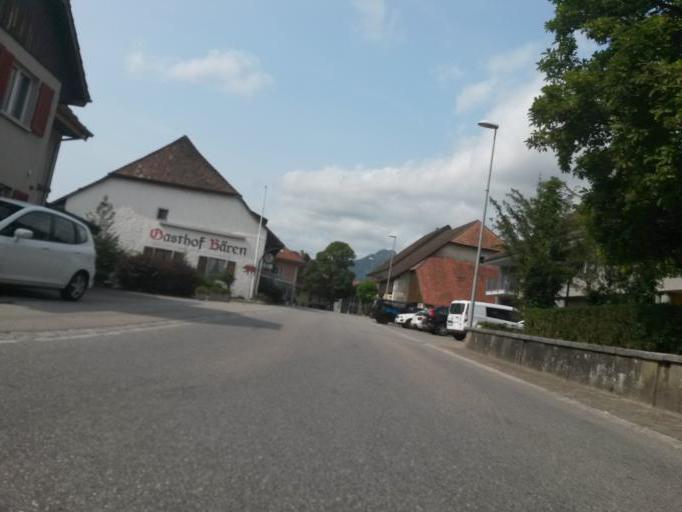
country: CH
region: Bern
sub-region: Oberaargau
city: Attiswil
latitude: 47.2472
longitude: 7.6146
